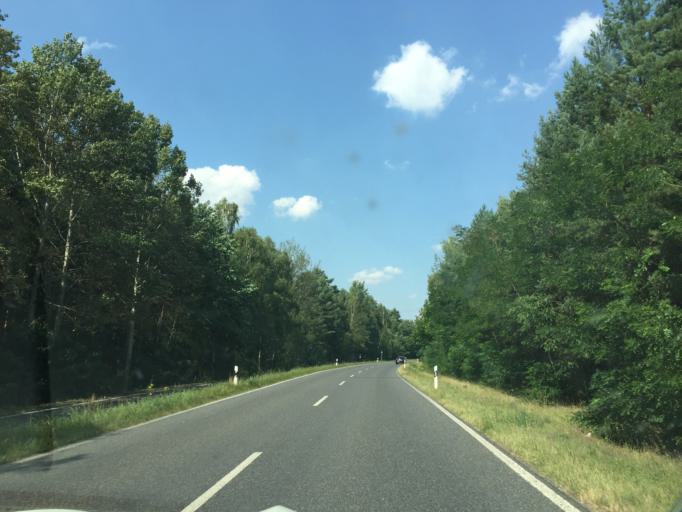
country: DE
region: Saxony
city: Boxberg
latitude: 51.4194
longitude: 14.5484
